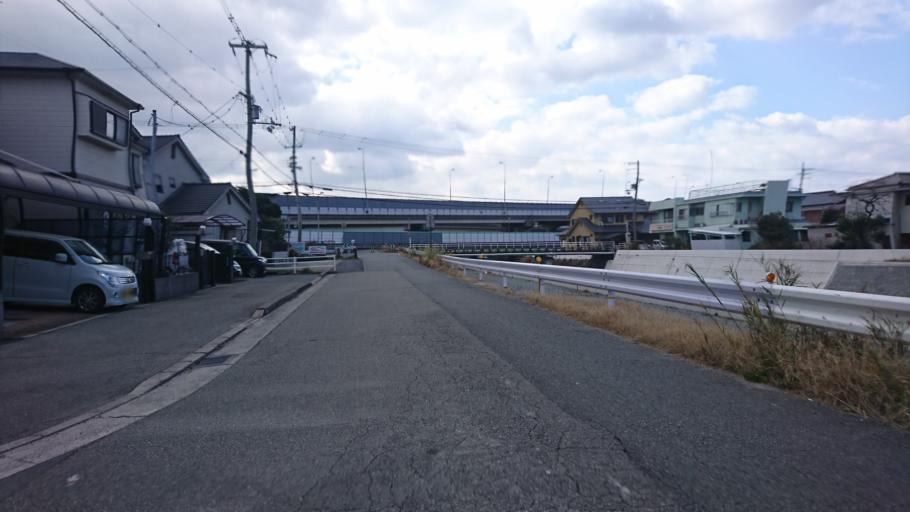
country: JP
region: Hyogo
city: Kakogawacho-honmachi
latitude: 34.7923
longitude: 134.8004
